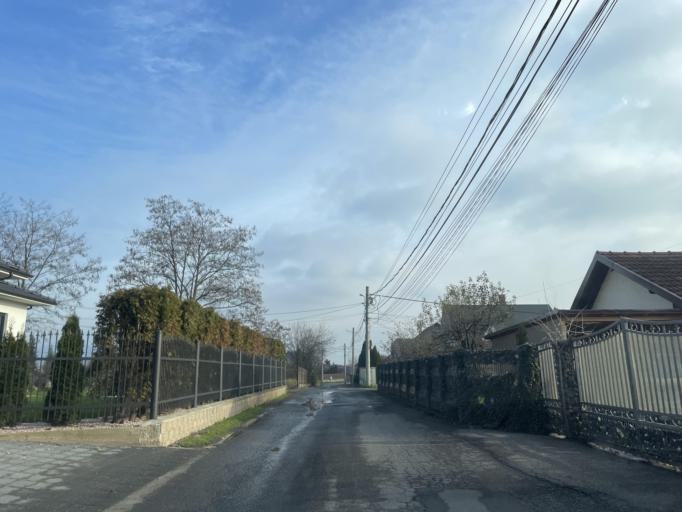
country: RO
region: Mures
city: Reghin-Sat
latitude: 46.7927
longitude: 24.7063
